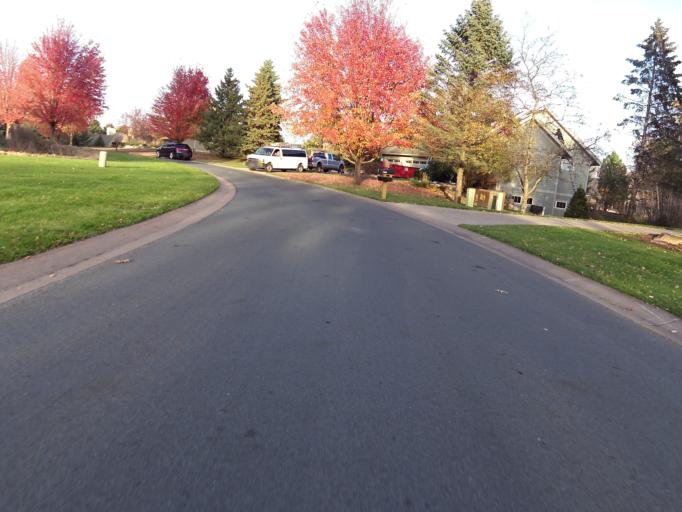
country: US
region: Minnesota
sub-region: Washington County
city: Lake Elmo
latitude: 44.9690
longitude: -92.8811
